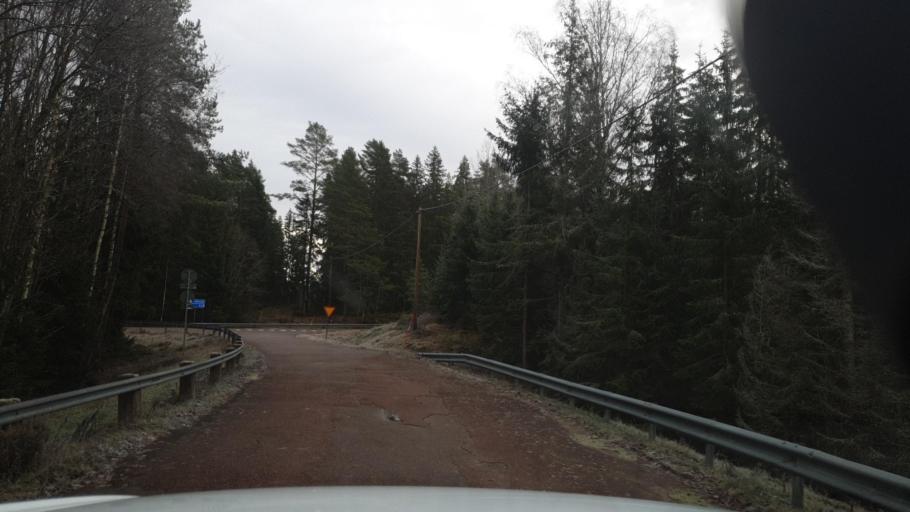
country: SE
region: Vaermland
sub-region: Karlstads Kommun
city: Edsvalla
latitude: 59.6079
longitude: 12.9893
